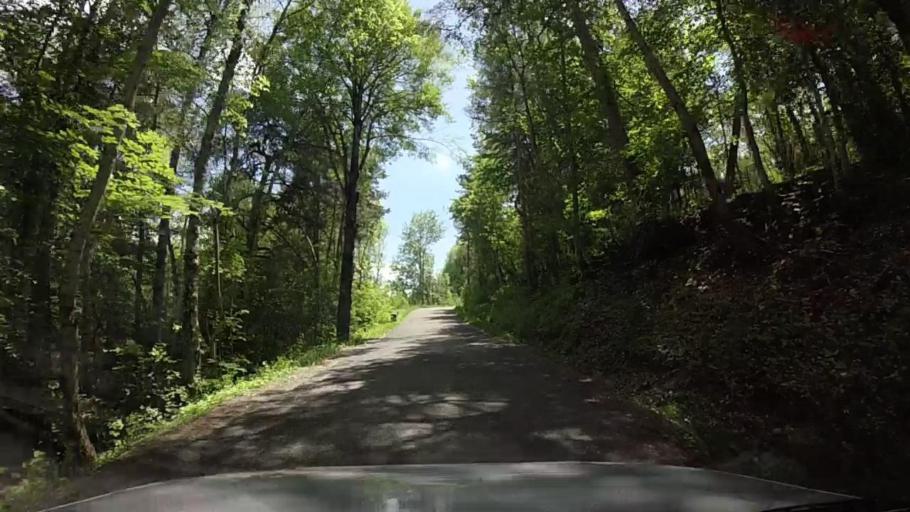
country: FR
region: Provence-Alpes-Cote d'Azur
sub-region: Departement des Alpes-de-Haute-Provence
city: Seyne-les-Alpes
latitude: 44.3346
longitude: 6.3447
